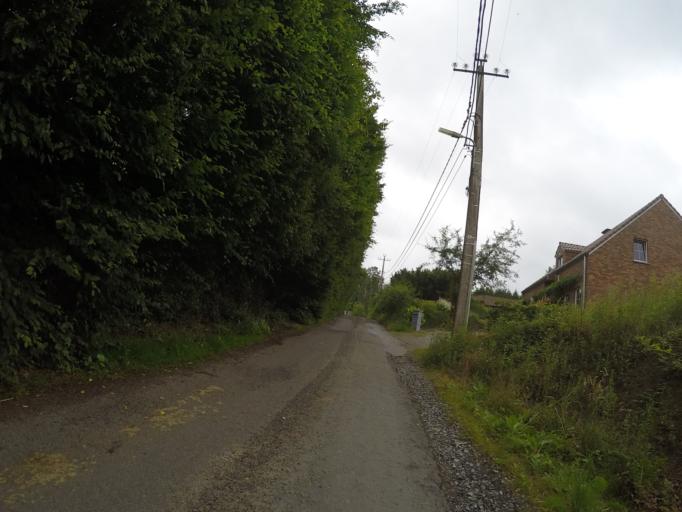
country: BE
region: Wallonia
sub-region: Province de Namur
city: Yvoir
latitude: 50.3314
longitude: 4.9275
